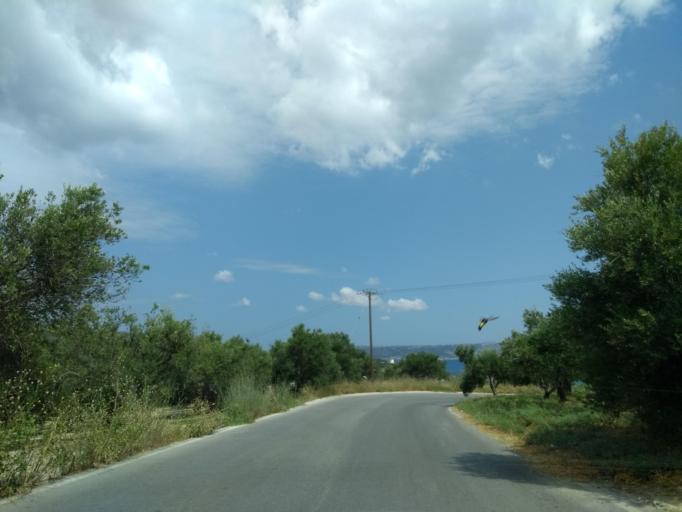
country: GR
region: Crete
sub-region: Nomos Chanias
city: Kalivai
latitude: 35.4451
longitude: 24.1751
